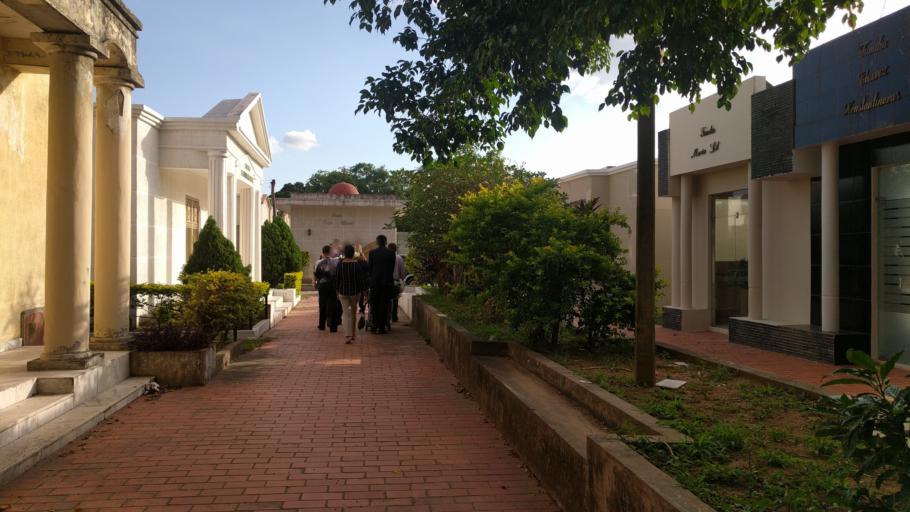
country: BO
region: Santa Cruz
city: Santa Cruz de la Sierra
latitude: -17.7480
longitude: -63.1612
